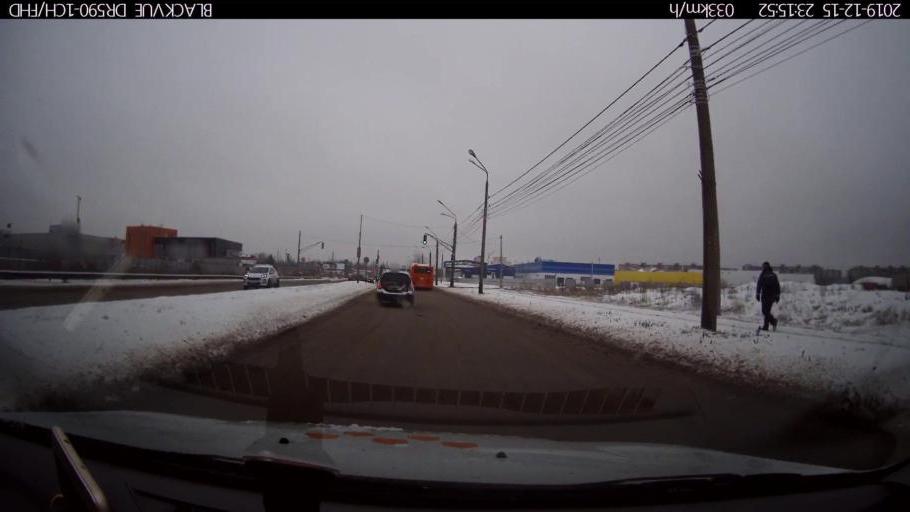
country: RU
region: Nizjnij Novgorod
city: Neklyudovo
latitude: 56.3427
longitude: 43.8887
